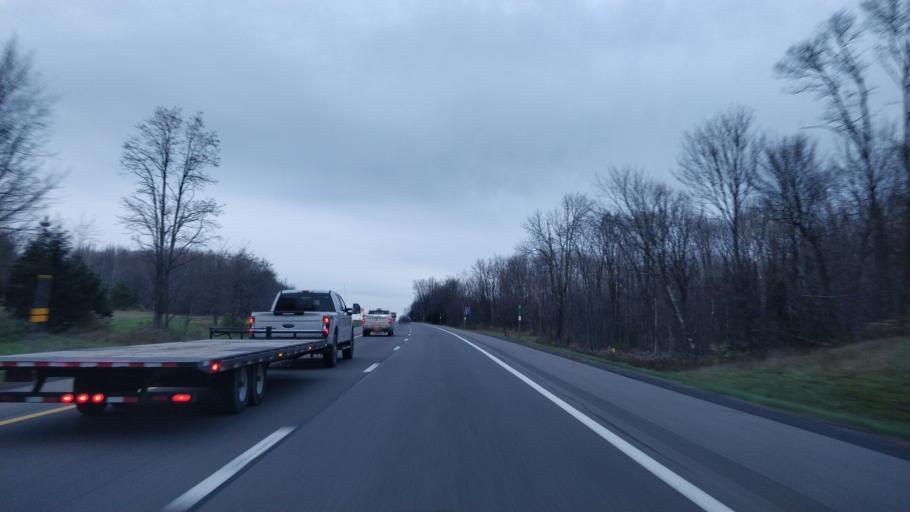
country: US
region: New York
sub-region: Oswego County
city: Central Square
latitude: 43.3641
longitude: -76.1203
